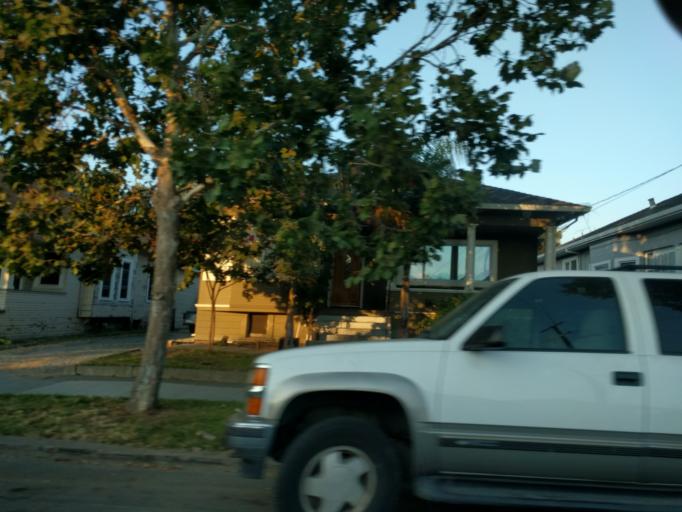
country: US
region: California
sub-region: Santa Clara County
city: San Jose
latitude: 37.3477
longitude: -121.8823
